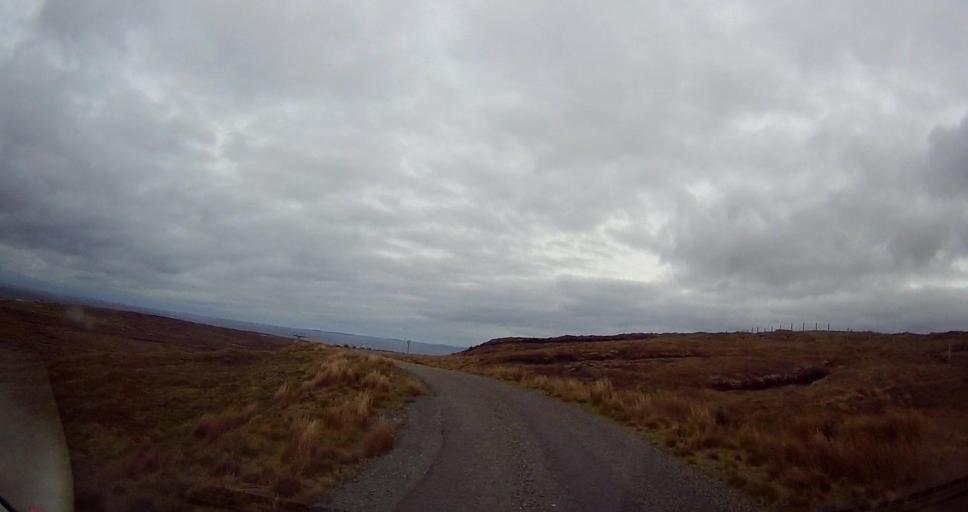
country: GB
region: Scotland
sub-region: Shetland Islands
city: Shetland
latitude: 60.5626
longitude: -1.0636
